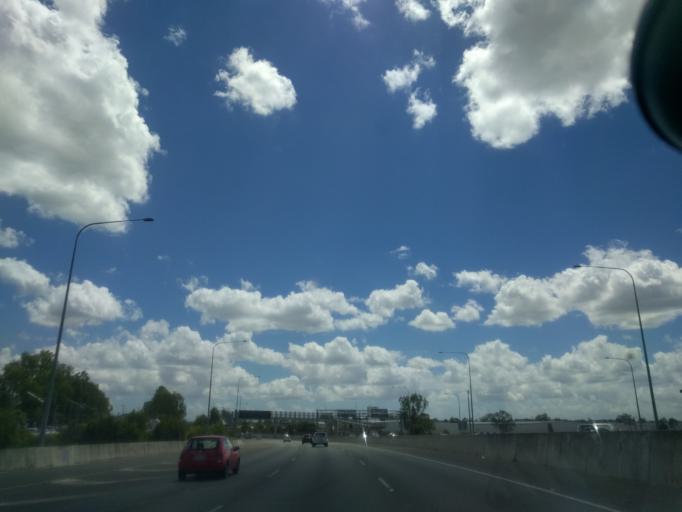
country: AU
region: Queensland
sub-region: Brisbane
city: Wacol
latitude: -27.6038
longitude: 152.9185
